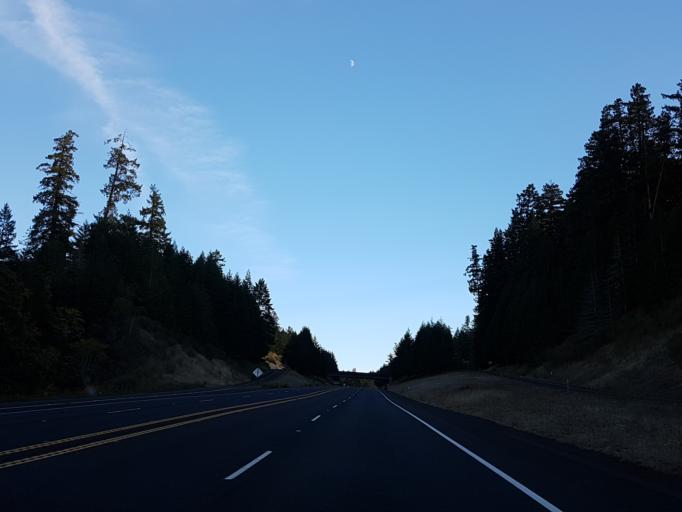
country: US
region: California
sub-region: Humboldt County
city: Redway
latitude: 39.9476
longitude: -123.7809
